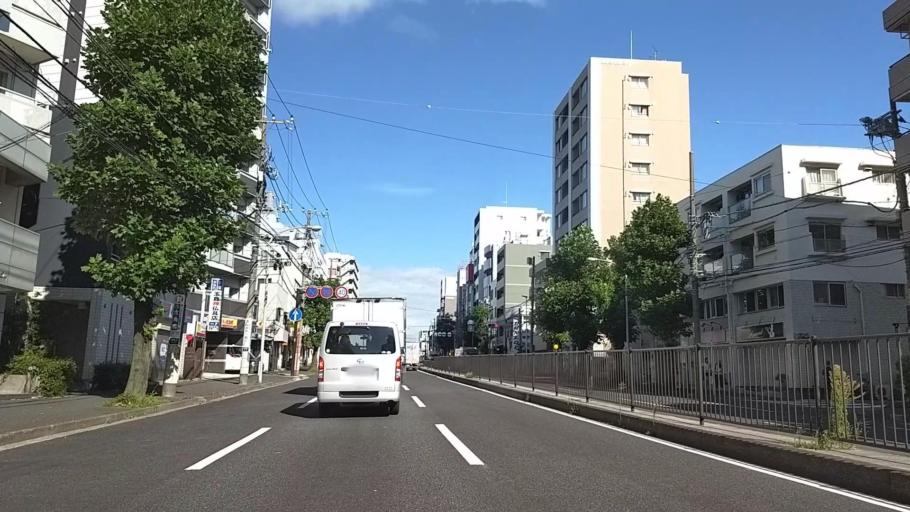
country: JP
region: Kanagawa
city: Yokohama
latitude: 35.4842
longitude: 139.6282
